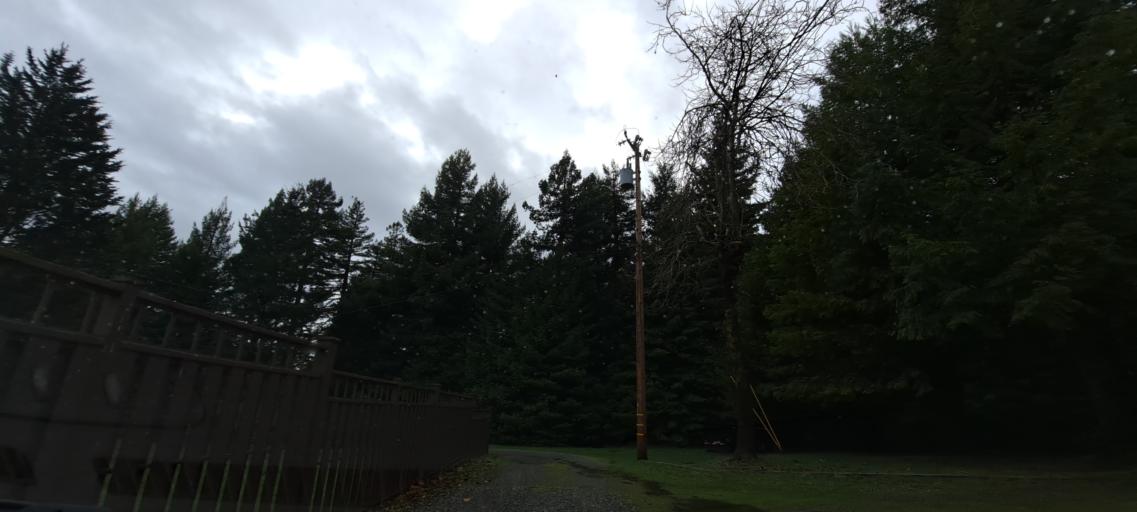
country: US
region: California
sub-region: Humboldt County
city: Fortuna
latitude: 40.6048
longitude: -124.1414
